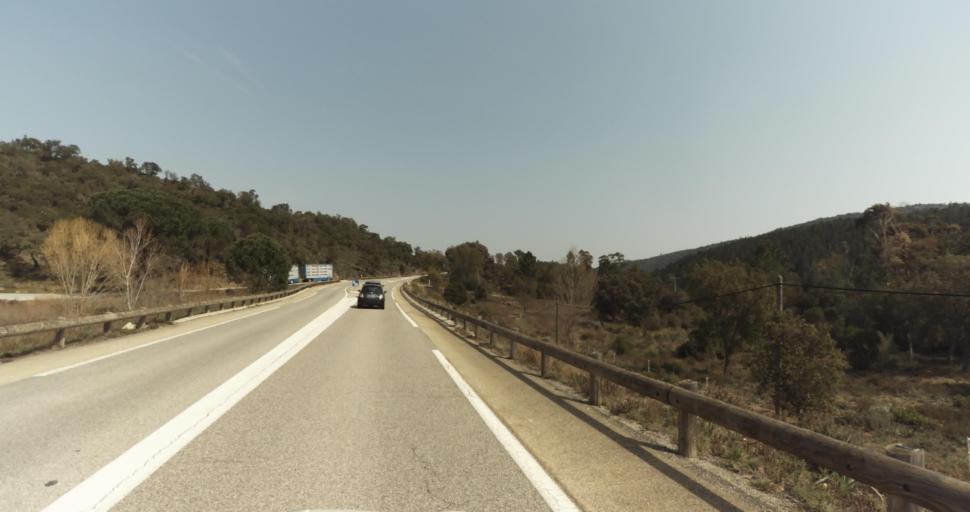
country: FR
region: Provence-Alpes-Cote d'Azur
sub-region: Departement du Var
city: Le Lavandou
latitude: 43.1882
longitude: 6.3647
